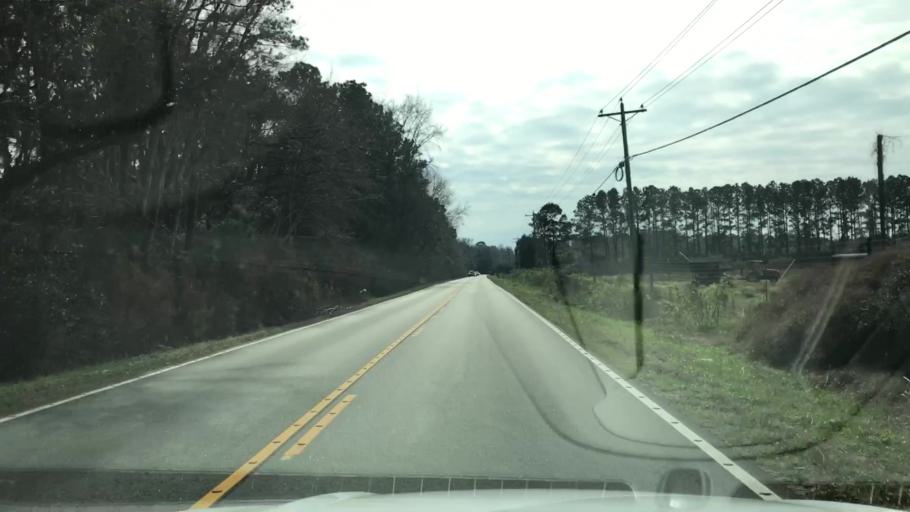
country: US
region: South Carolina
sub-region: Charleston County
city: Shell Point
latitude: 32.7238
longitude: -80.0232
